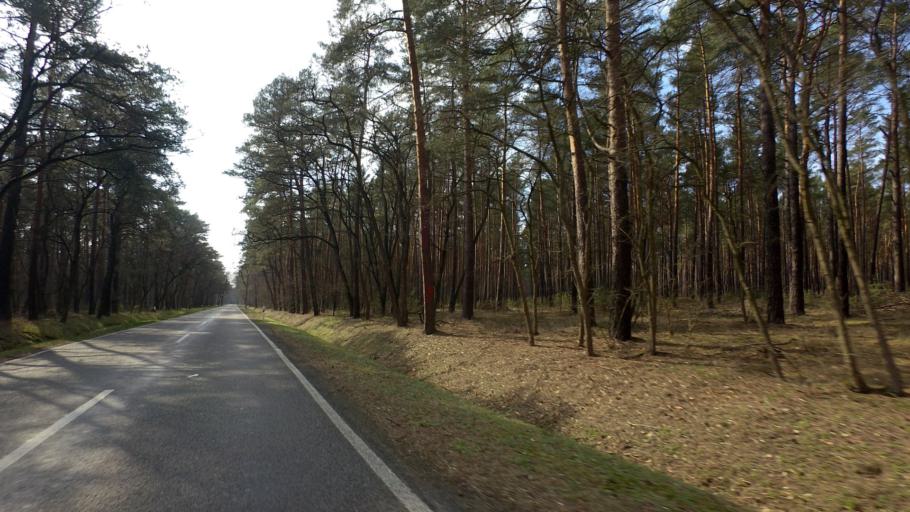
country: DE
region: Brandenburg
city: Dahme
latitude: 51.9526
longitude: 13.4103
